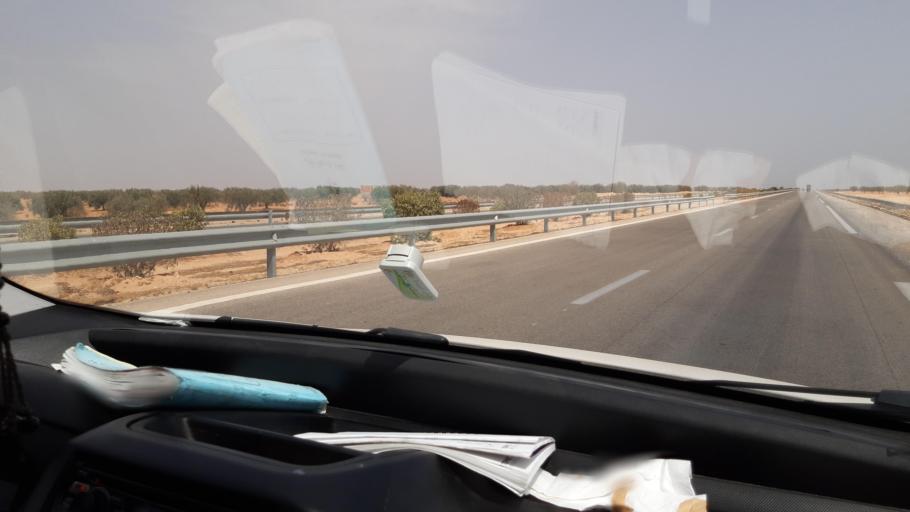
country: TN
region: Safaqis
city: Bi'r `Ali Bin Khalifah
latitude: 34.5660
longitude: 10.3589
